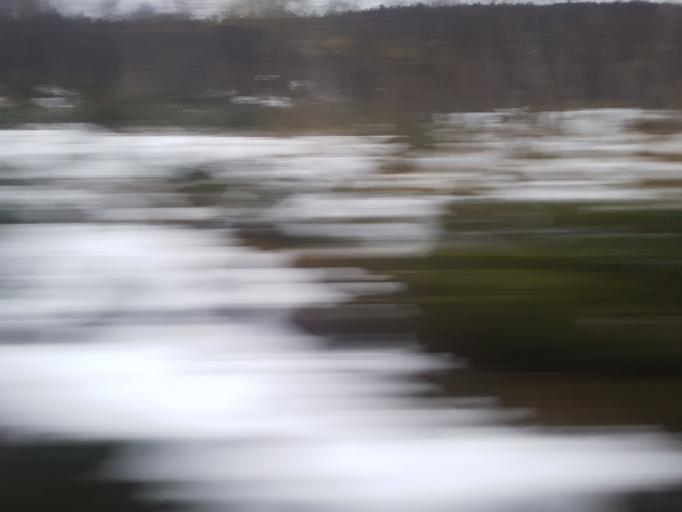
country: NO
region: Sor-Trondelag
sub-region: Oppdal
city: Oppdal
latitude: 62.3353
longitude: 9.6221
